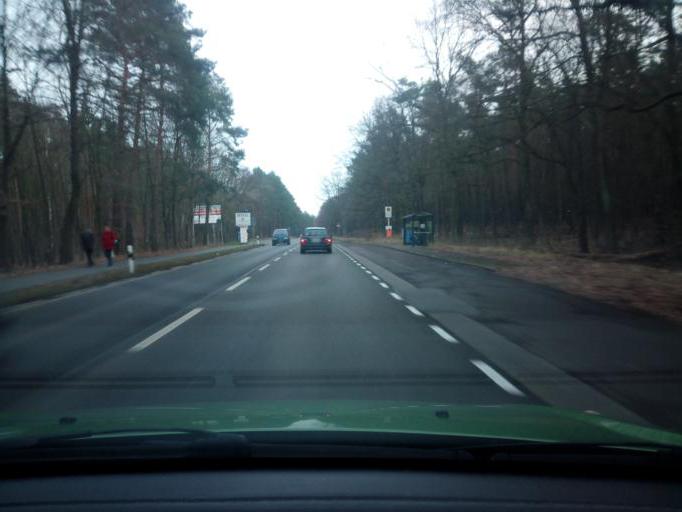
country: DE
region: Berlin
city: Muggelheim
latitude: 52.4220
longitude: 13.6398
